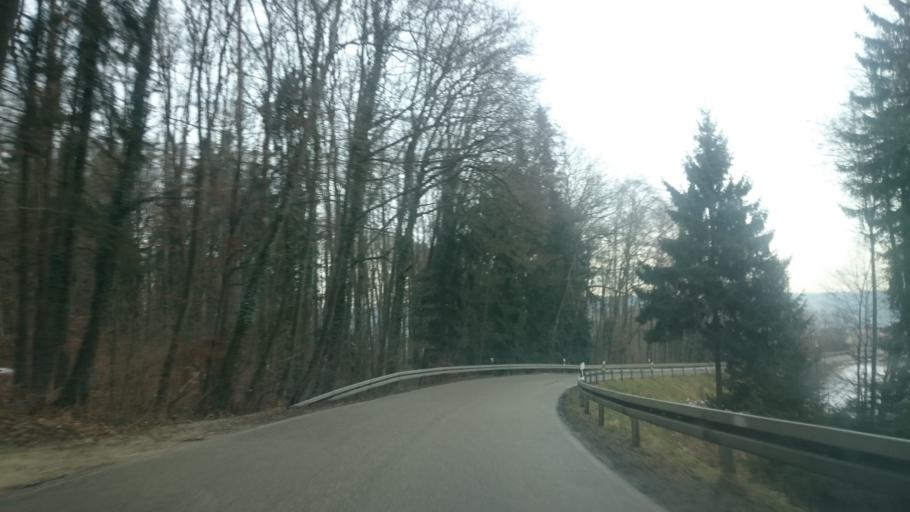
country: DE
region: Bavaria
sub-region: Regierungsbezirk Mittelfranken
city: Thalmassing
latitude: 49.0809
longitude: 11.2025
